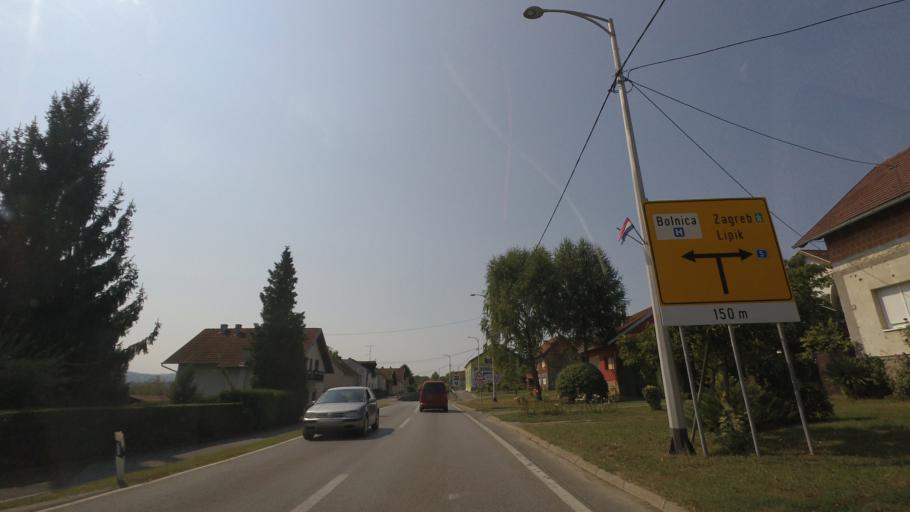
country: HR
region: Pozesko-Slavonska
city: Pakrac
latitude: 45.4293
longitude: 17.1847
